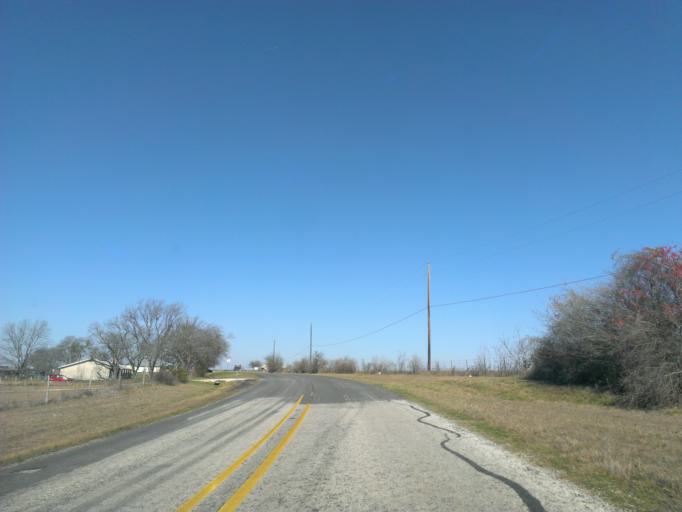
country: US
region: Texas
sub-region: Williamson County
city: Serenada
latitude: 30.7125
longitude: -97.5776
